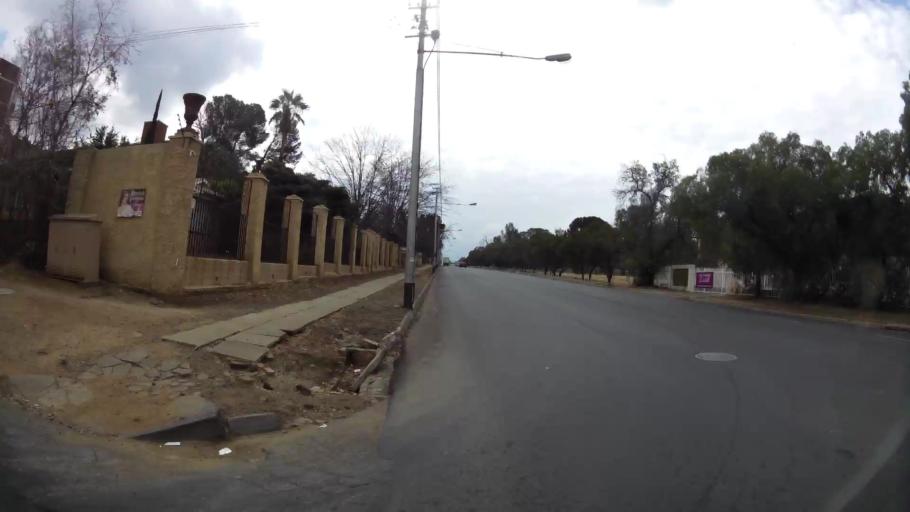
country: ZA
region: Orange Free State
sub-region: Mangaung Metropolitan Municipality
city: Bloemfontein
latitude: -29.1080
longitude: 26.2205
